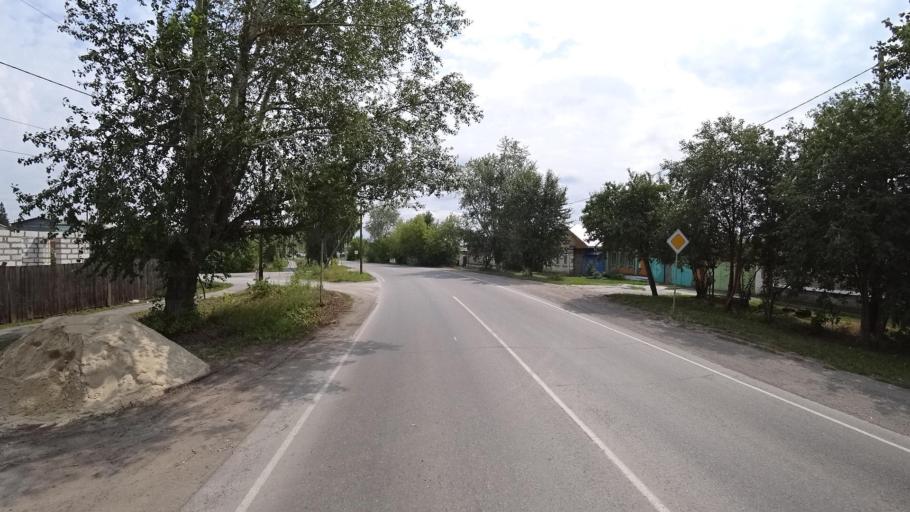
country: RU
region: Sverdlovsk
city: Kamyshlov
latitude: 56.8465
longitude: 62.6784
